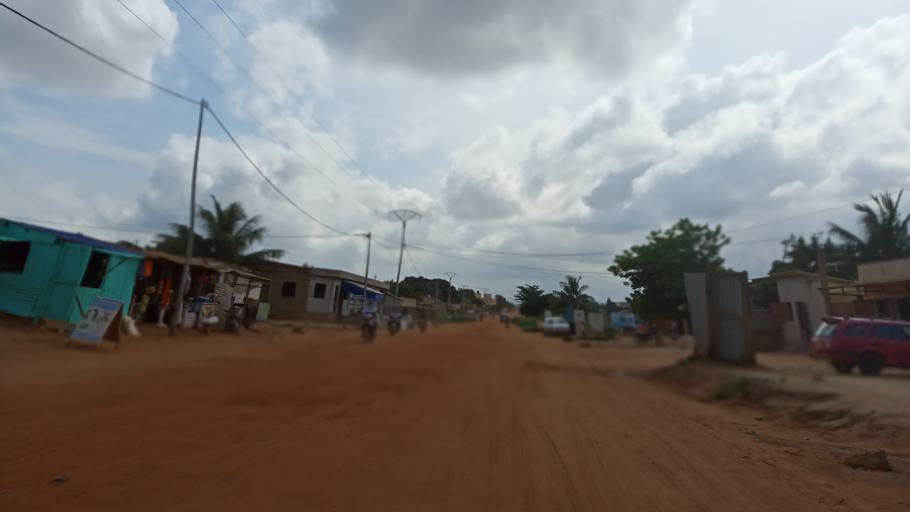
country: TG
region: Maritime
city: Lome
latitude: 6.2334
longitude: 1.1411
